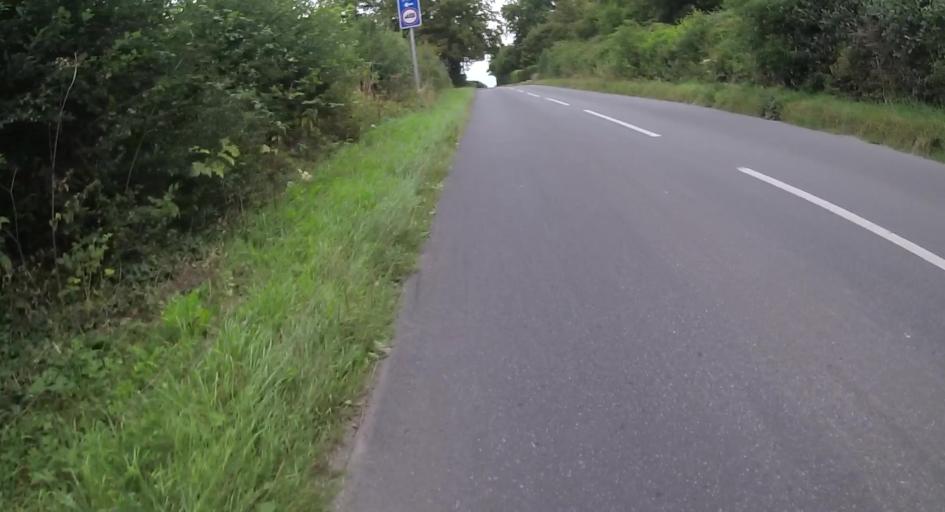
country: GB
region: England
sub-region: Hampshire
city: Kings Worthy
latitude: 51.1233
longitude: -1.3103
